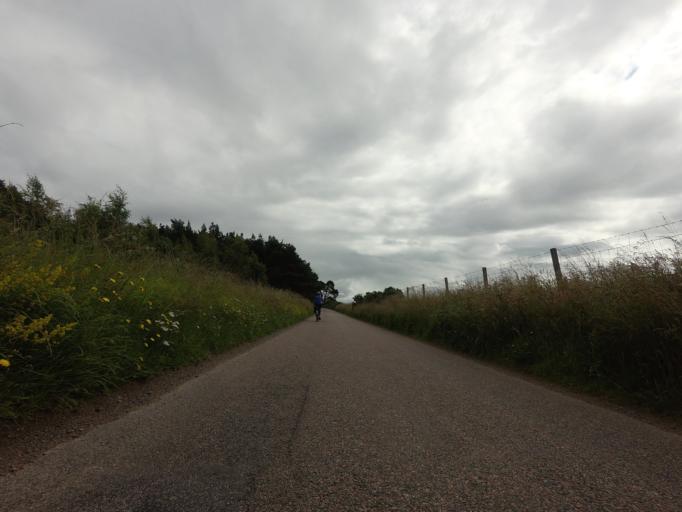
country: GB
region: Scotland
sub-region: Moray
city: Lhanbryd
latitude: 57.6676
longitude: -3.1652
